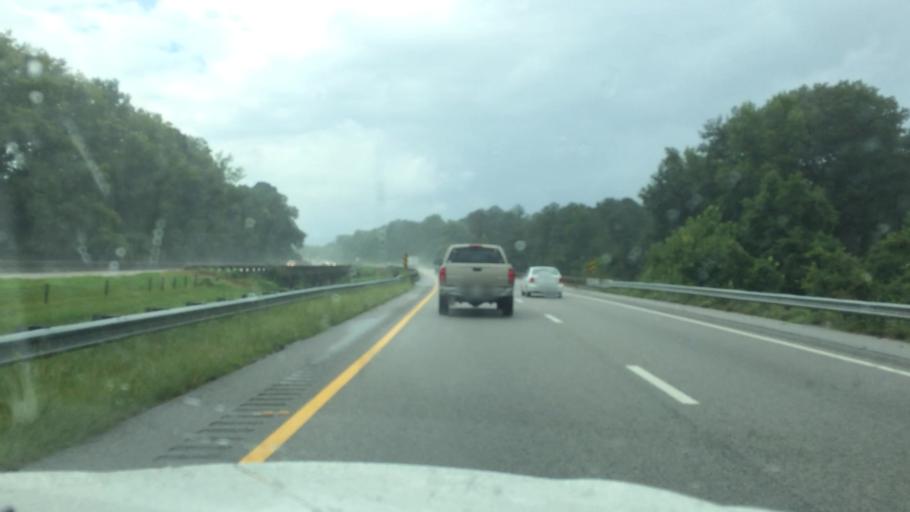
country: US
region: South Carolina
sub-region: Kershaw County
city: Camden
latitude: 34.2197
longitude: -80.6176
